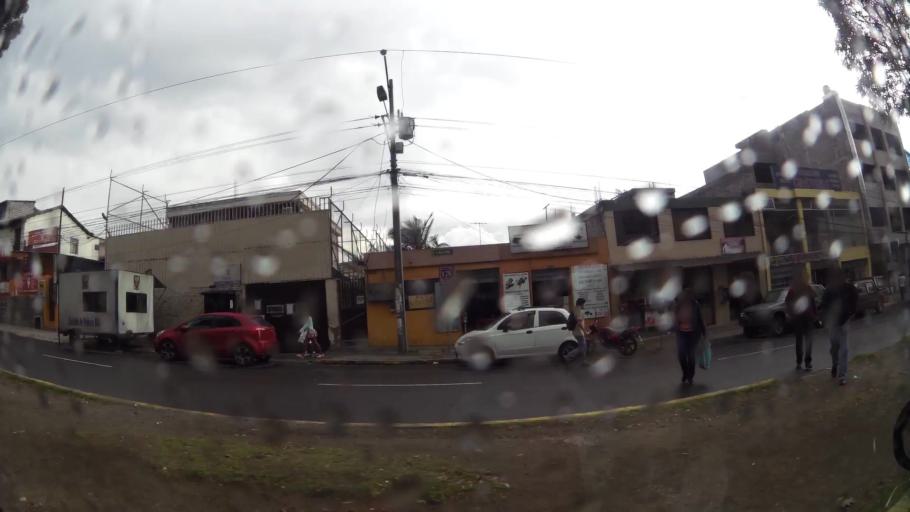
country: EC
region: Pichincha
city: Quito
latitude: -0.1041
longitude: -78.4915
